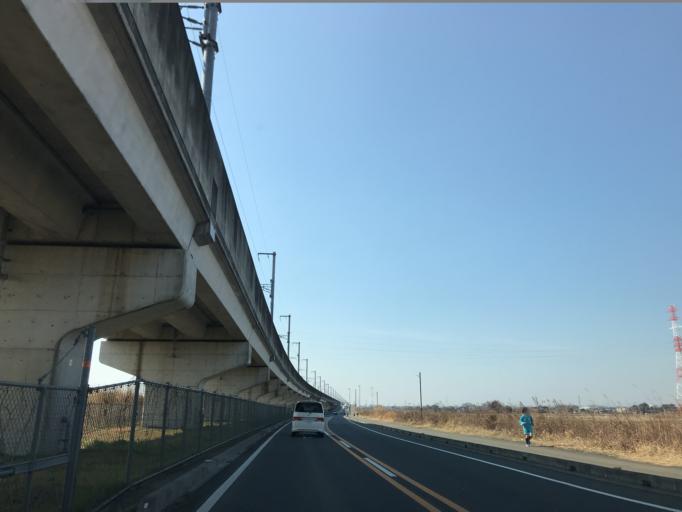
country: JP
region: Ibaraki
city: Mitsukaido
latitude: 35.9852
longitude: 140.0322
